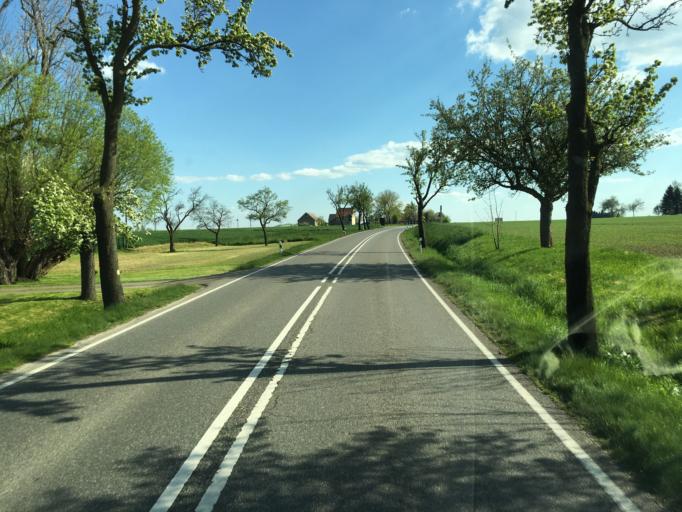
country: DE
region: Saxony
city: Ebersbach
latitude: 51.0822
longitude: 13.1106
